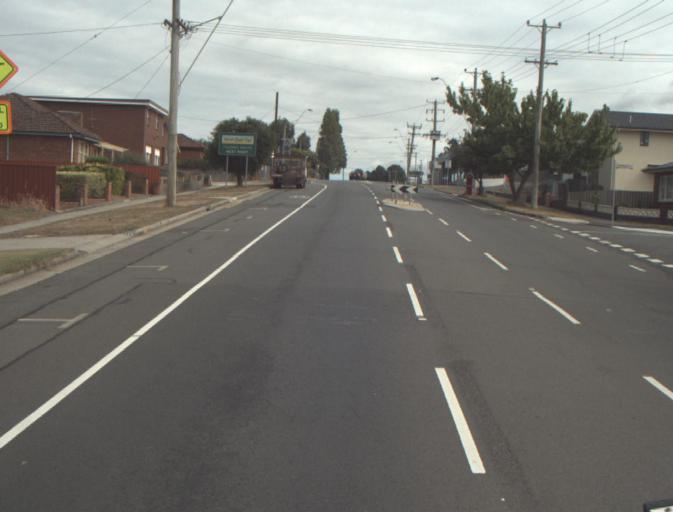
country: AU
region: Tasmania
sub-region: Launceston
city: Mayfield
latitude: -41.3800
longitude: 147.1279
